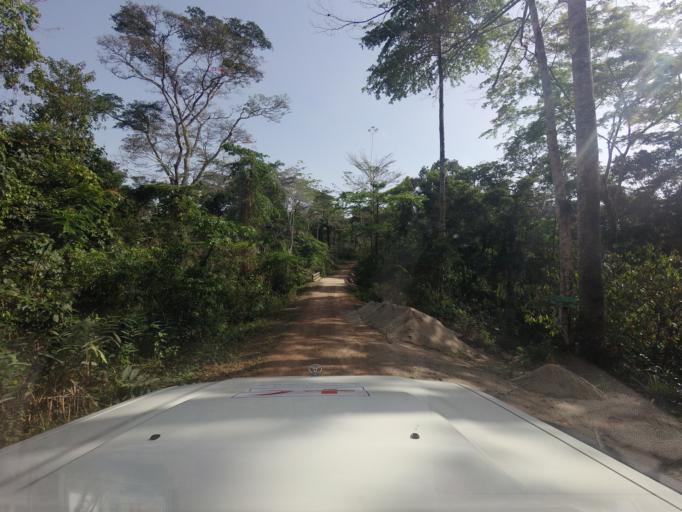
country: LR
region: Lofa
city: Voinjama
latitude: 8.5183
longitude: -9.7602
